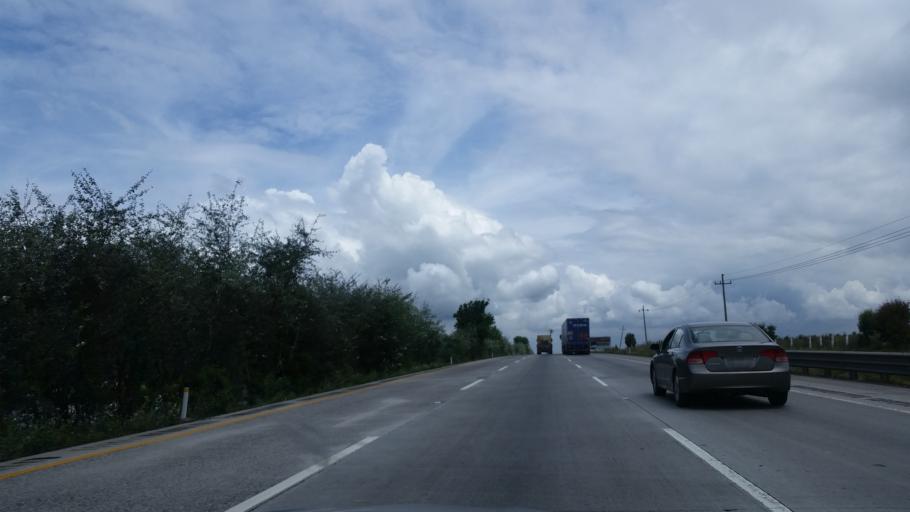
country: MX
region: Mexico
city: San Francisco Soyaniquilpan
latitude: 19.9952
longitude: -99.4799
